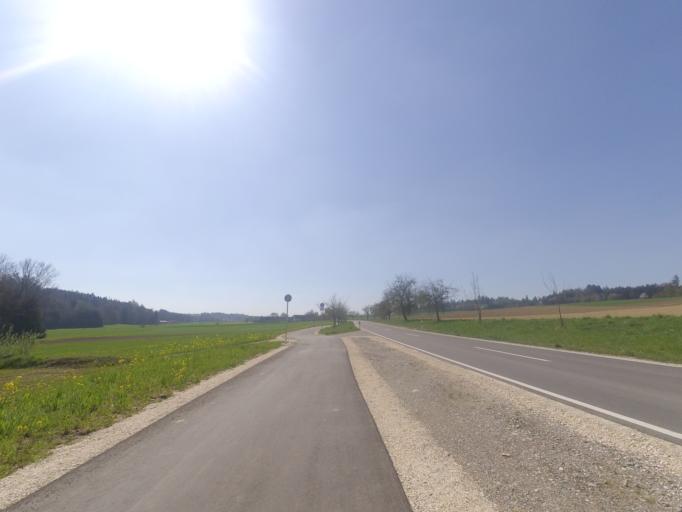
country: DE
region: Bavaria
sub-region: Swabia
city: Roggenburg
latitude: 48.3054
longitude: 10.2105
